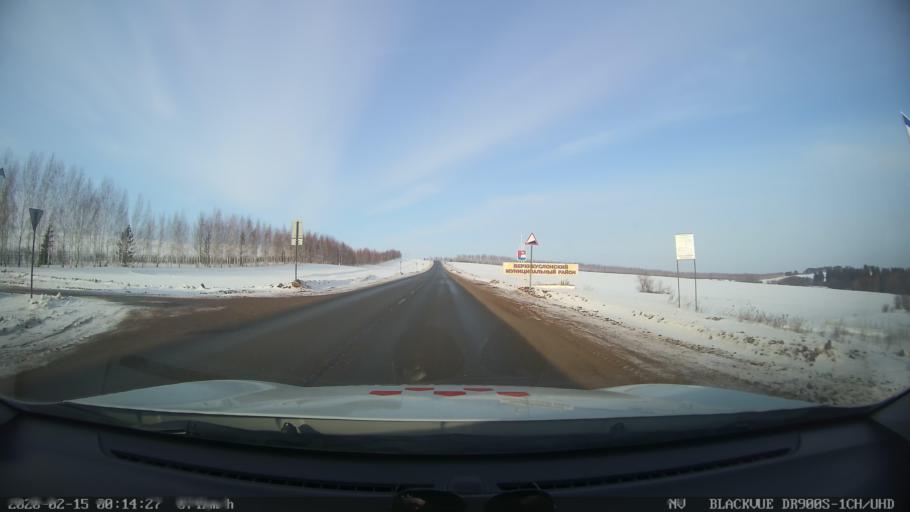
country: RU
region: Tatarstan
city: Stolbishchi
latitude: 55.4861
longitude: 49.0044
